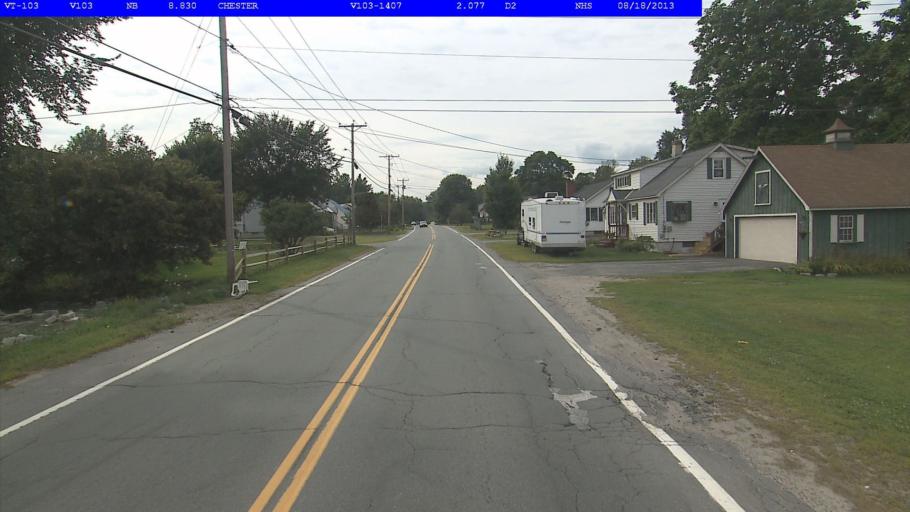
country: US
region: Vermont
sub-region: Windsor County
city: Chester
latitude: 43.2562
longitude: -72.5807
